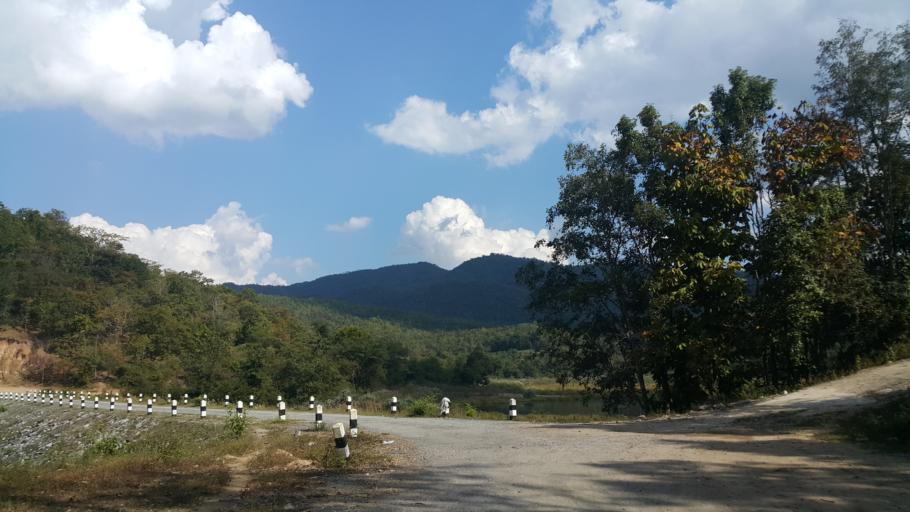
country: TH
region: Lamphun
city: Ban Thi
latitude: 18.5849
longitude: 99.1600
